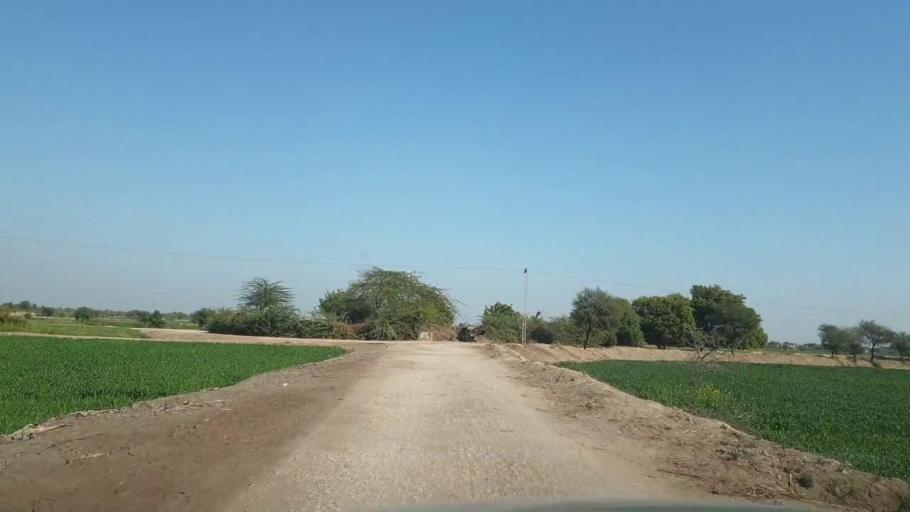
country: PK
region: Sindh
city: Tando Adam
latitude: 25.6624
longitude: 68.6924
